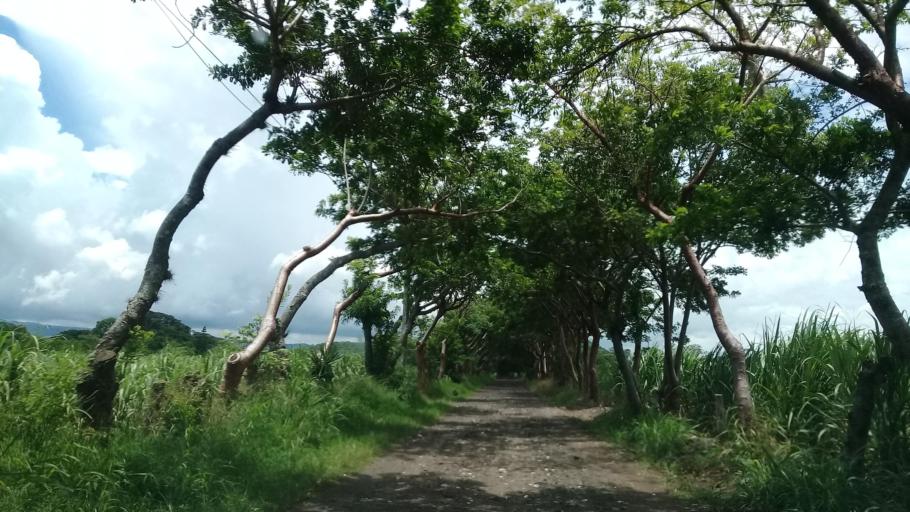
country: MX
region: Veracruz
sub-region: Naolinco
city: El Espinal
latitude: 19.5884
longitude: -96.8609
